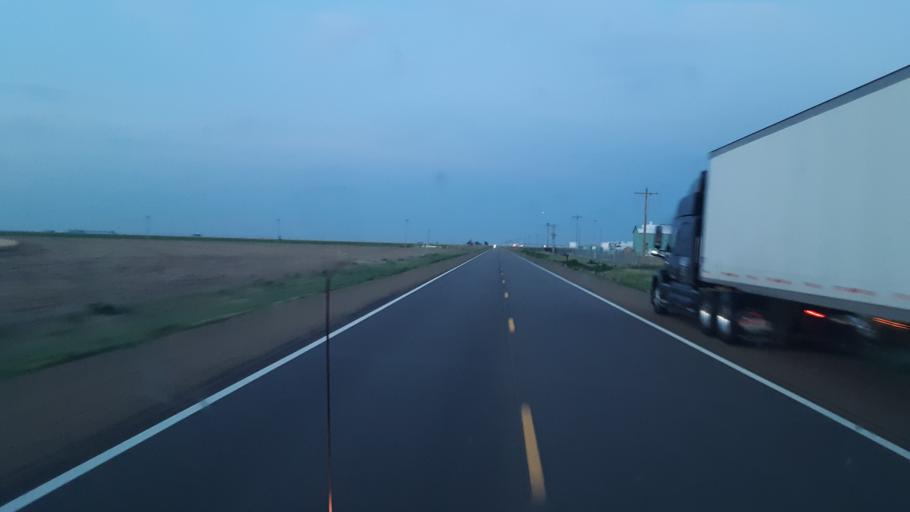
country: US
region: Kansas
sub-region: Finney County
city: Holcomb
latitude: 38.0034
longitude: -101.0521
